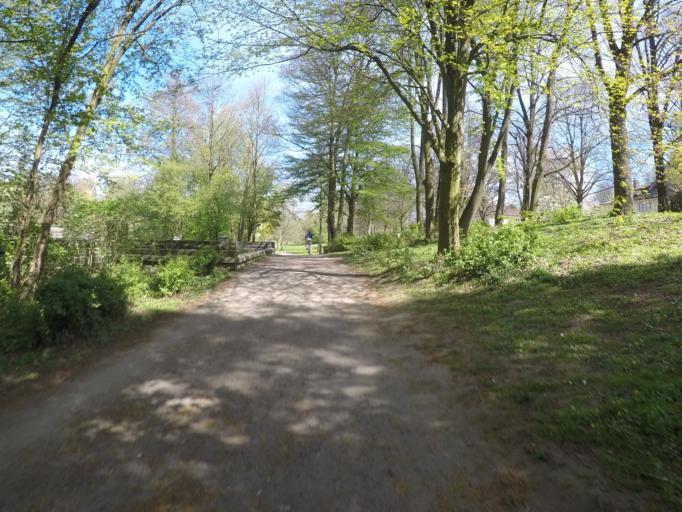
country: DE
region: Hamburg
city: Alsterdorf
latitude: 53.6168
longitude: 10.0217
